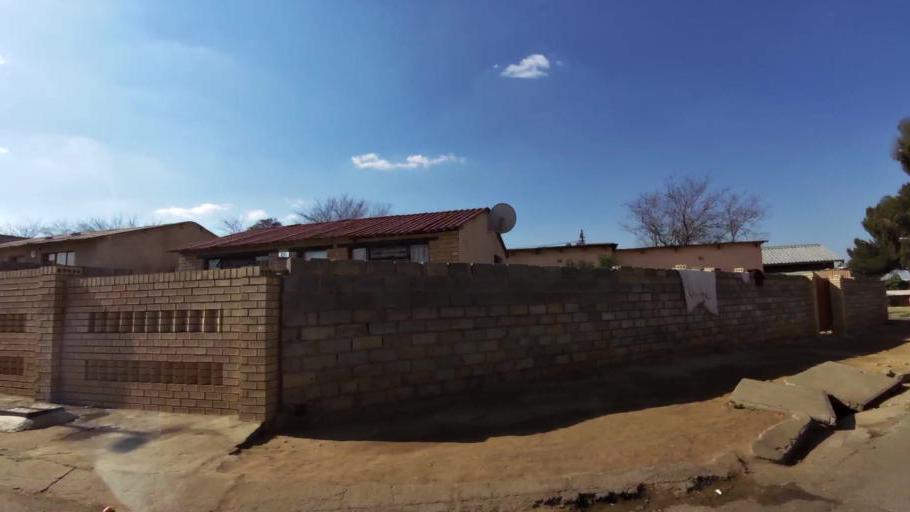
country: ZA
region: Gauteng
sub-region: City of Johannesburg Metropolitan Municipality
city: Soweto
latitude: -26.2380
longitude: 27.8779
